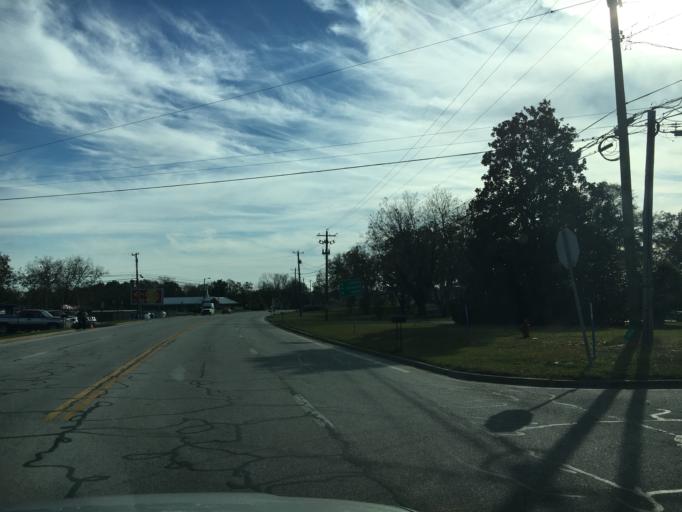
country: US
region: Georgia
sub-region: Elbert County
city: Elberton
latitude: 34.1281
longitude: -82.8594
